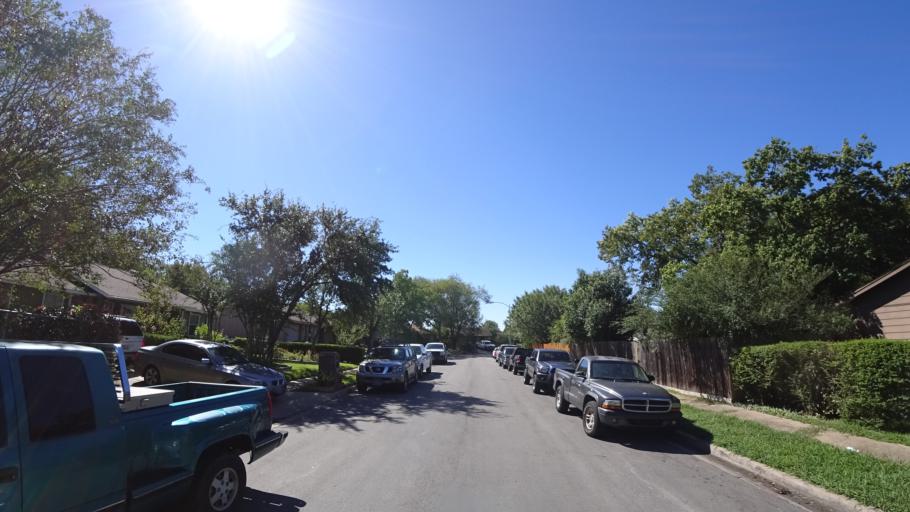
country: US
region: Texas
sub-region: Travis County
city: Hornsby Bend
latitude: 30.3033
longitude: -97.6450
